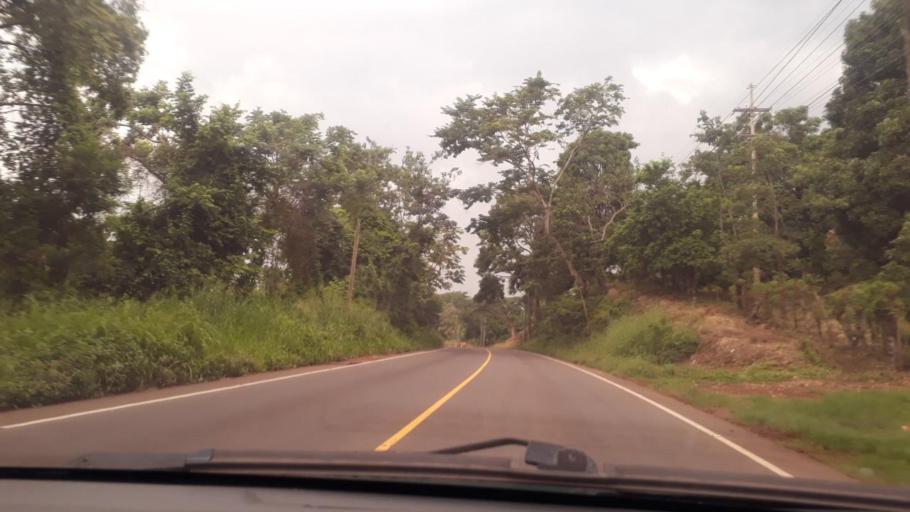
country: GT
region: Santa Rosa
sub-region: Municipio de Taxisco
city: Taxisco
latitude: 14.0671
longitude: -90.4429
